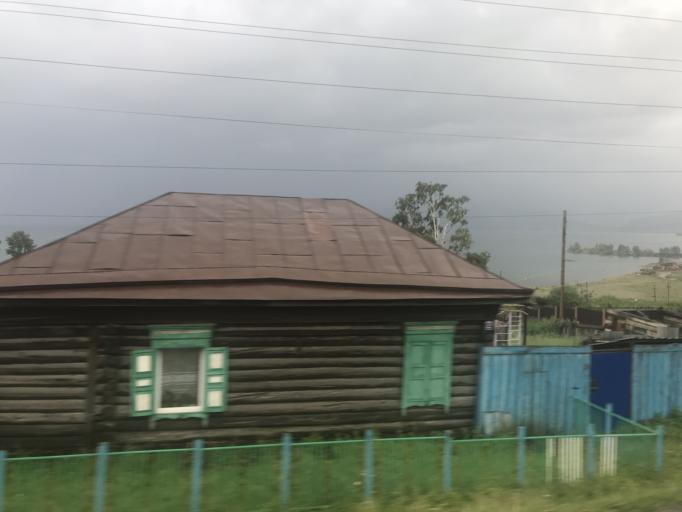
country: RU
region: Irkutsk
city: Kultuk
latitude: 51.7306
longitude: 103.7200
